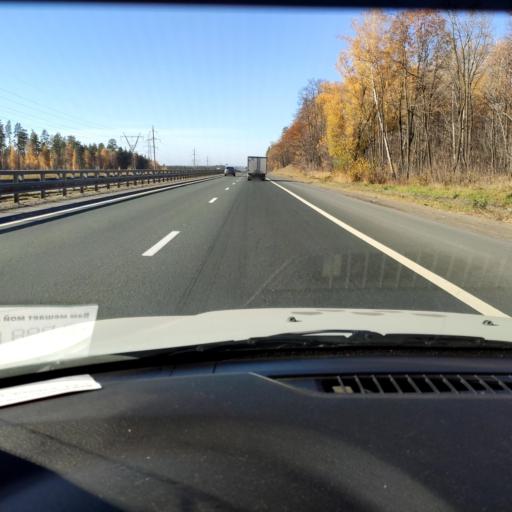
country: RU
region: Samara
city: Povolzhskiy
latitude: 53.5176
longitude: 49.7908
